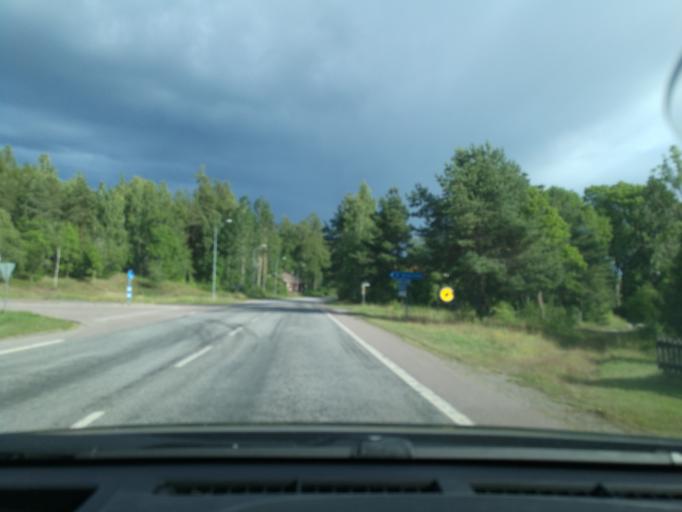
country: SE
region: Vaestmanland
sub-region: Surahammars Kommun
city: Ramnas
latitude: 59.7658
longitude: 16.2066
